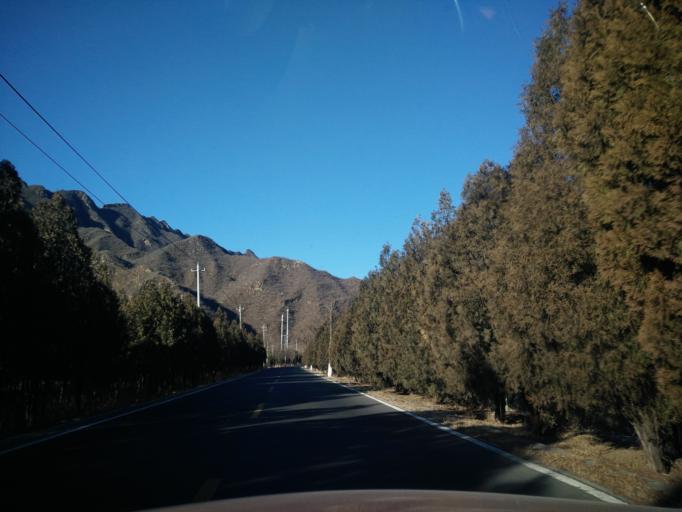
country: CN
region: Beijing
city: Wangping
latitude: 40.0051
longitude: 115.9980
